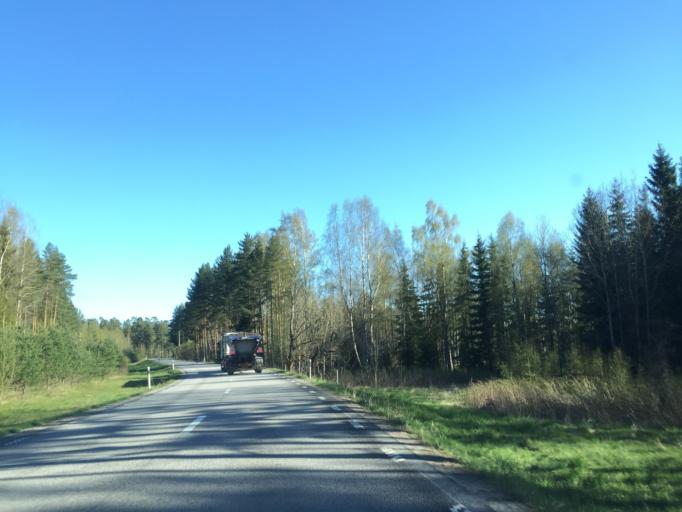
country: SE
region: OErebro
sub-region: Hallsbergs Kommun
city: Skollersta
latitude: 59.2402
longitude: 15.4033
